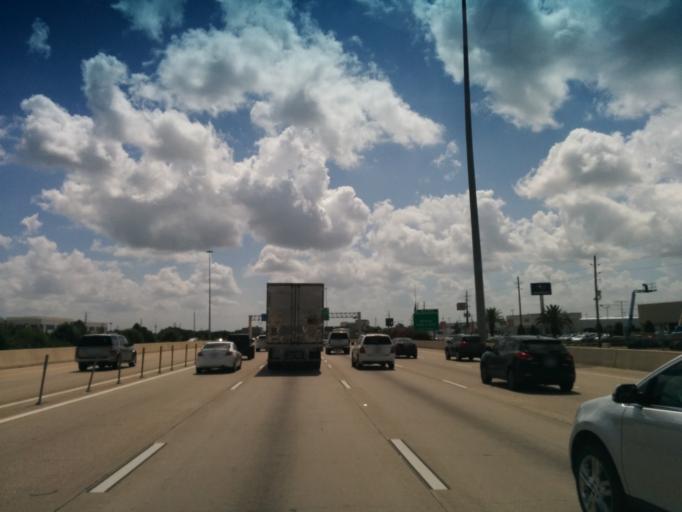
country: US
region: Texas
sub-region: Fort Bend County
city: Cinco Ranch
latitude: 29.7848
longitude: -95.6809
